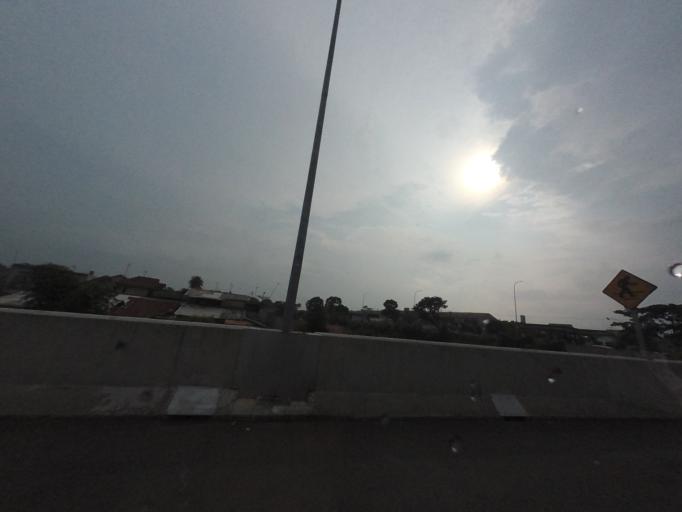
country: ID
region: West Java
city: Cicurug
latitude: -6.7520
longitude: 106.8004
